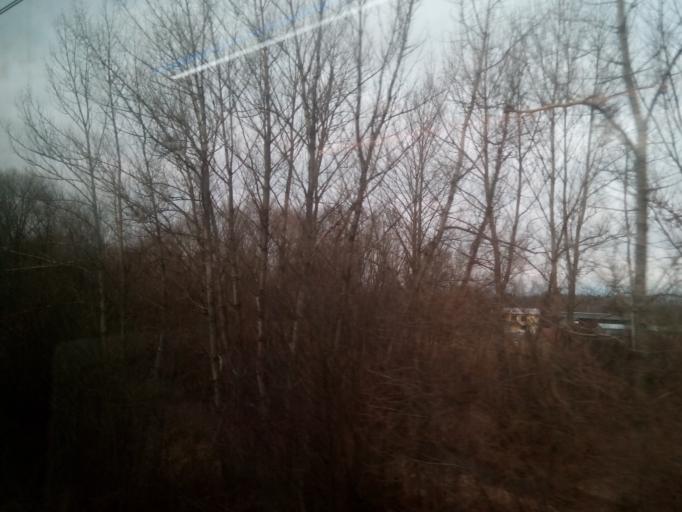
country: SK
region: Zilinsky
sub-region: Okres Liptovsky Mikulas
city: Liptovsky Mikulas
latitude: 49.0931
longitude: 19.5892
